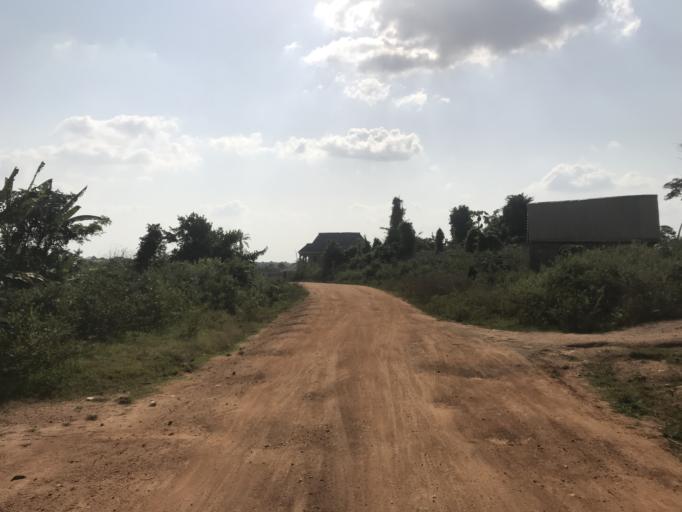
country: NG
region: Osun
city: Osogbo
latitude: 7.8232
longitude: 4.5665
